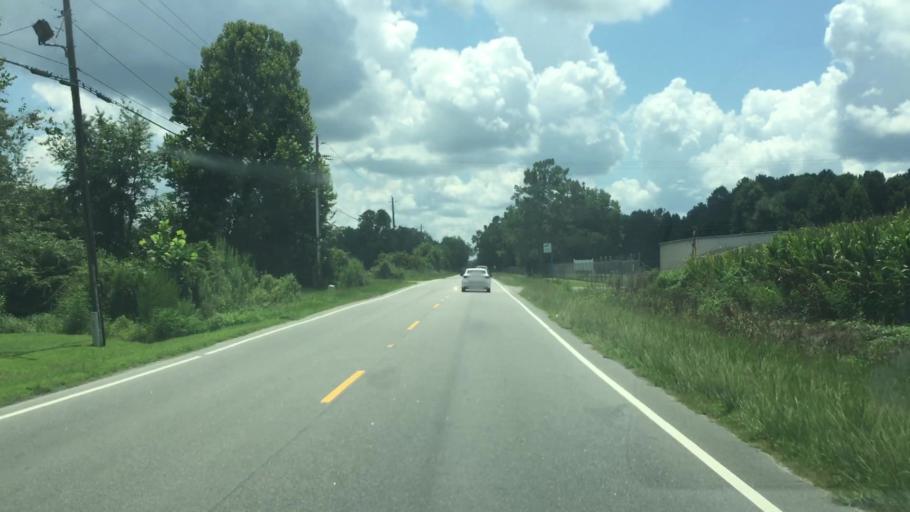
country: US
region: North Carolina
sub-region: Columbus County
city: Chadbourn
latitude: 34.3152
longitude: -78.8264
